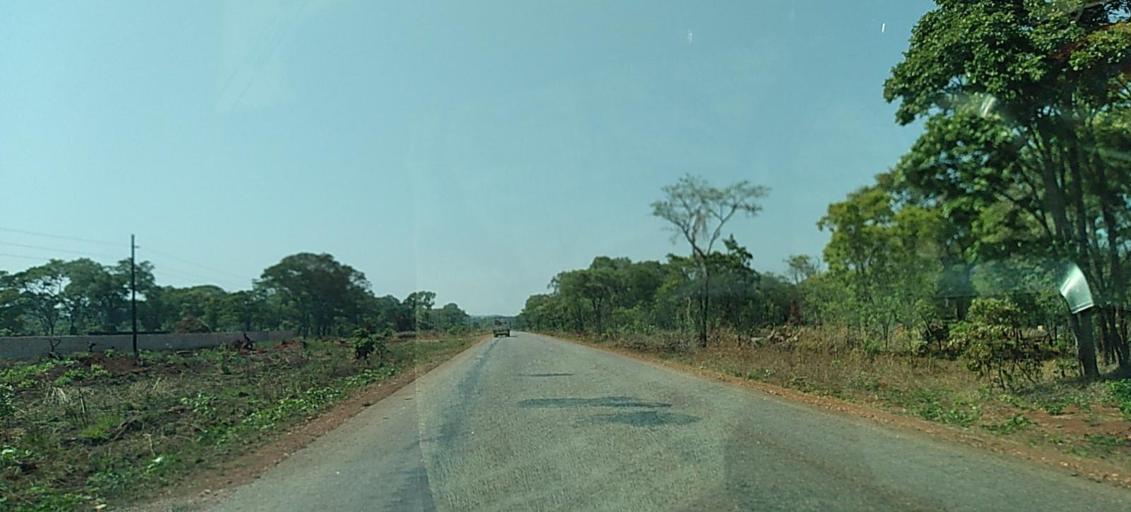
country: ZM
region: North-Western
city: Solwezi
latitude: -12.2032
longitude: 25.5555
